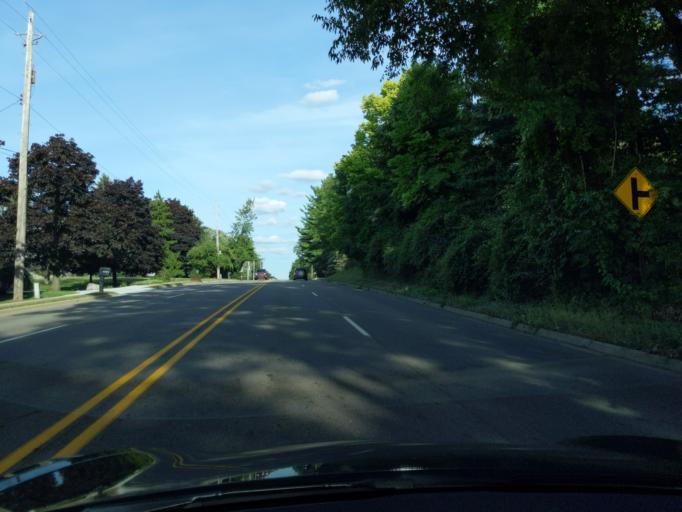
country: US
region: Michigan
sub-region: Eaton County
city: Waverly
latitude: 42.7266
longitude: -84.6534
